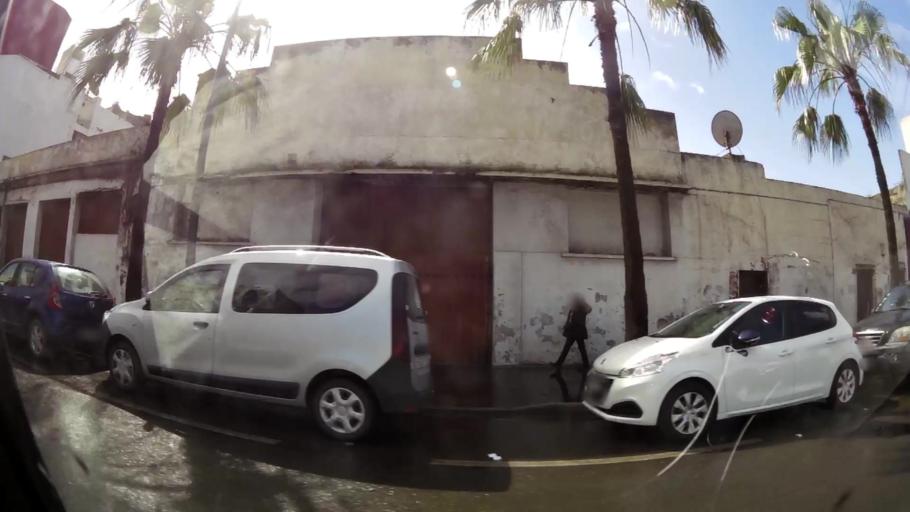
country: MA
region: Grand Casablanca
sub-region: Casablanca
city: Casablanca
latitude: 33.6018
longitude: -7.5842
